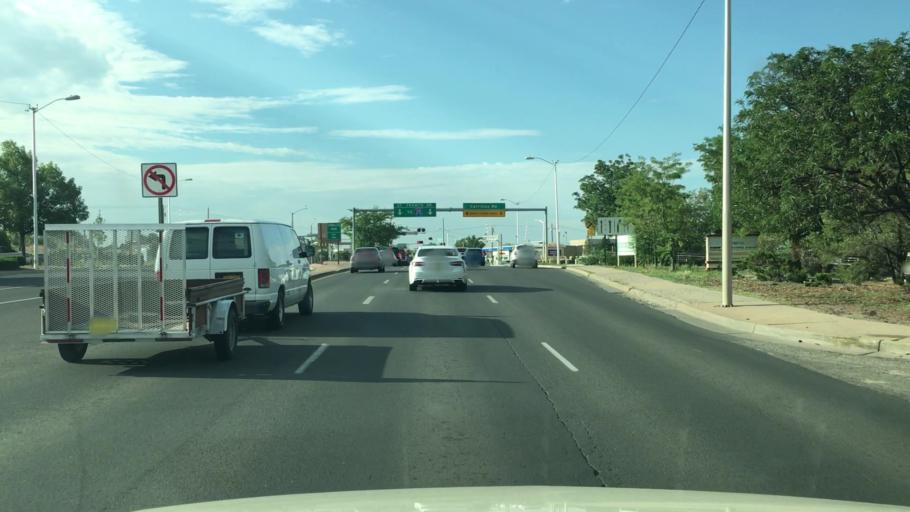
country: US
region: New Mexico
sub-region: Santa Fe County
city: Santa Fe
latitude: 35.6792
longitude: -105.9543
